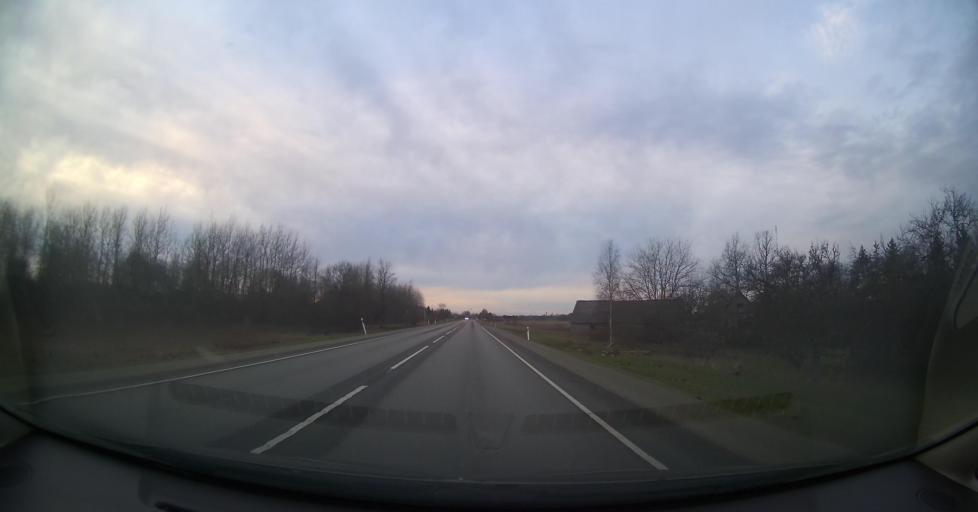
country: EE
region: Ida-Virumaa
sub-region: Kohtla-Jaerve linn
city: Kohtla-Jarve
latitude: 59.4203
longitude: 27.2112
